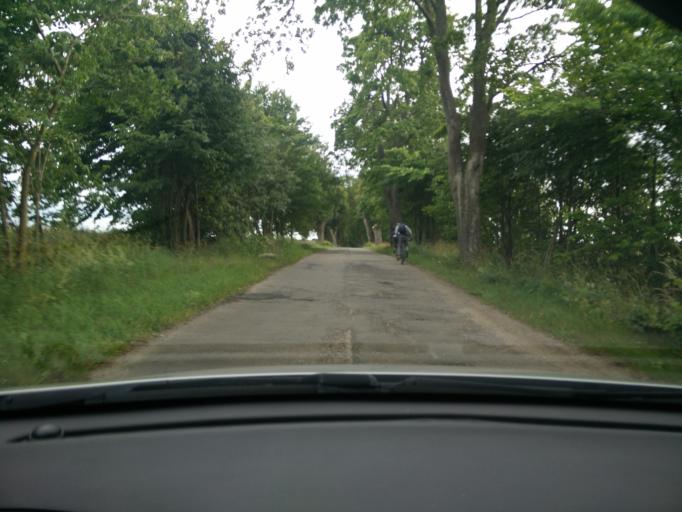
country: PL
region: Pomeranian Voivodeship
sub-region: Powiat pucki
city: Mrzezino
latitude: 54.6760
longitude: 18.4589
